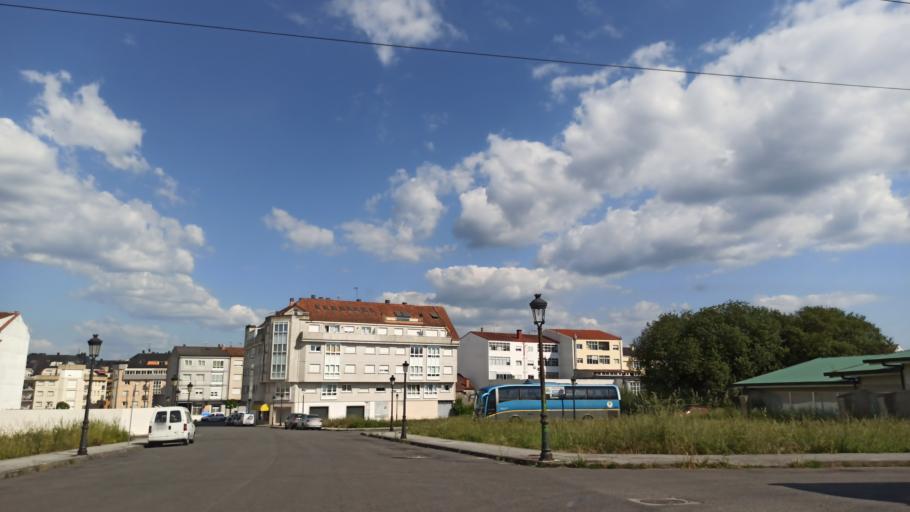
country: ES
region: Galicia
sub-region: Provincia da Coruna
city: Negreira
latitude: 42.9138
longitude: -8.7377
